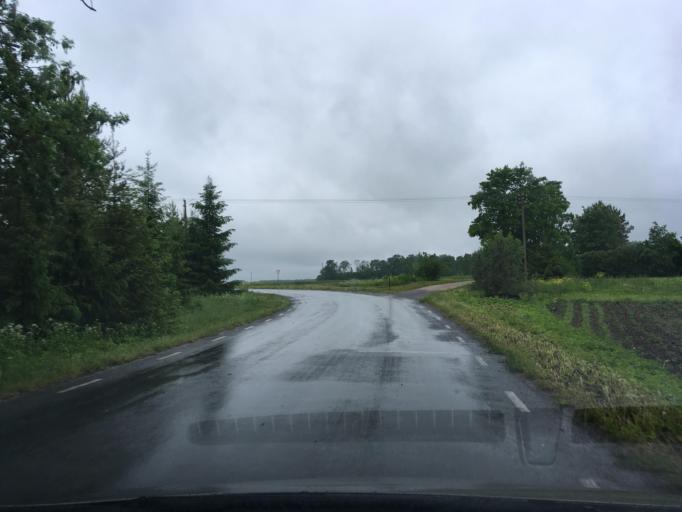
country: EE
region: Laeaene
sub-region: Lihula vald
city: Lihula
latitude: 58.6666
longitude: 23.7685
